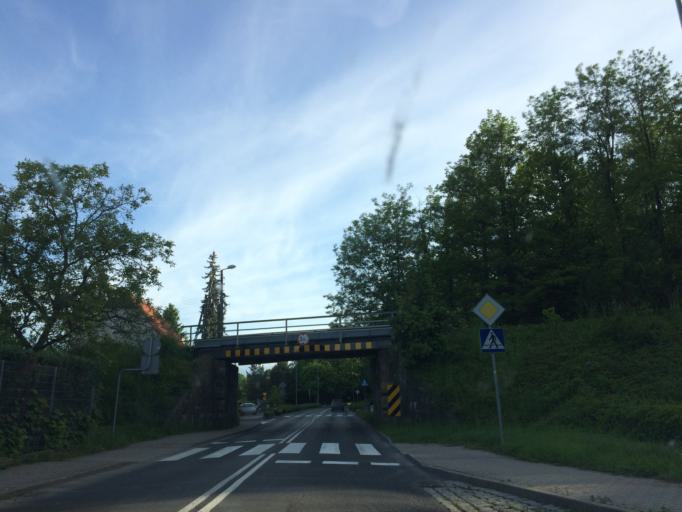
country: PL
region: Lower Silesian Voivodeship
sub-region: Powiat swidnicki
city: Swidnica
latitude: 50.8319
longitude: 16.4878
